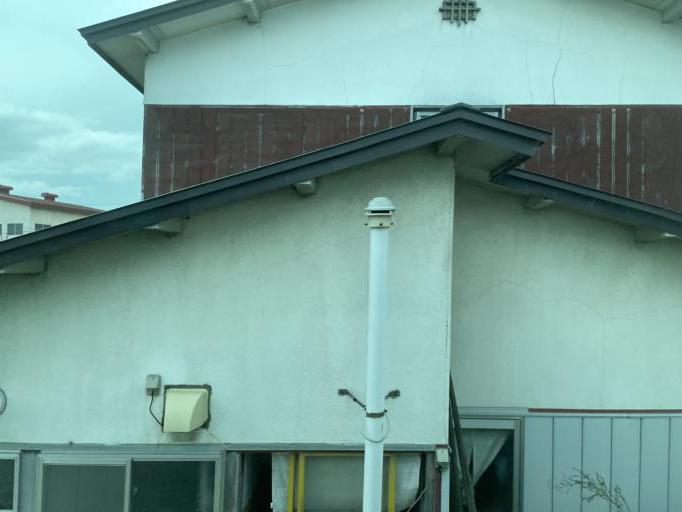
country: JP
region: Aomori
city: Goshogawara
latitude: 40.7654
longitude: 140.4350
